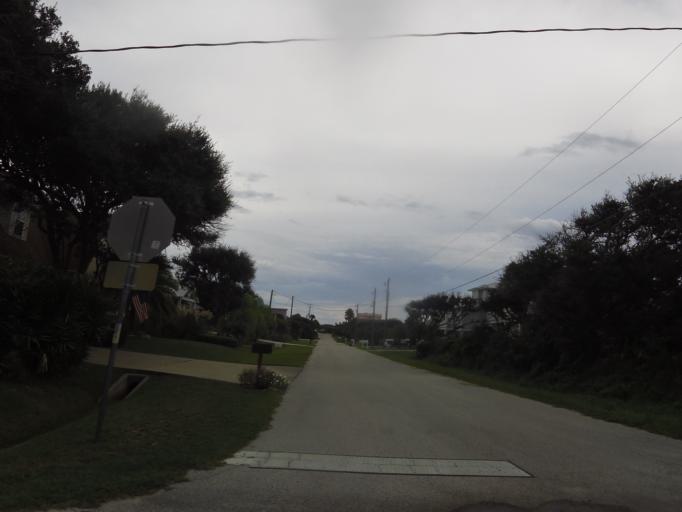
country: US
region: Florida
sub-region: Saint Johns County
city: Villano Beach
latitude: 29.9438
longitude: -81.3042
